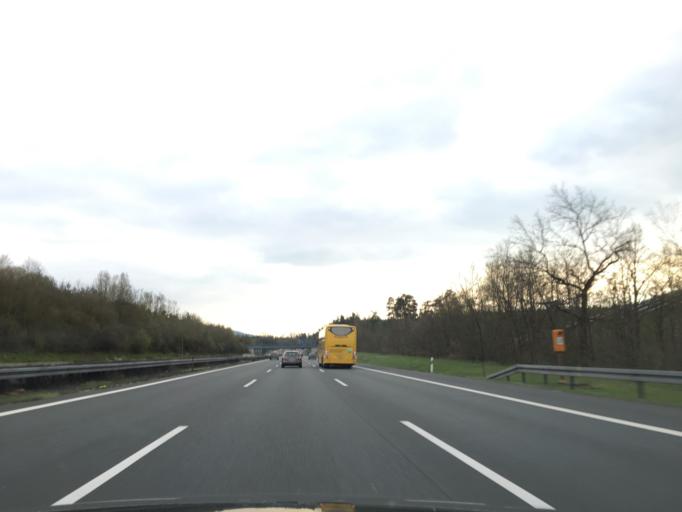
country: DE
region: Bavaria
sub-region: Regierungsbezirk Mittelfranken
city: Neunkirchen am Sand
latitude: 49.5348
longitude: 11.3172
